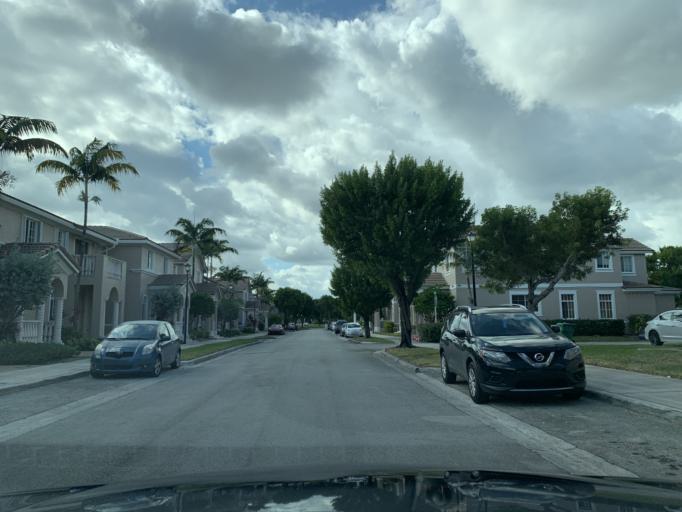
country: US
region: Florida
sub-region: Miami-Dade County
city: Naranja
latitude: 25.5074
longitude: -80.4179
